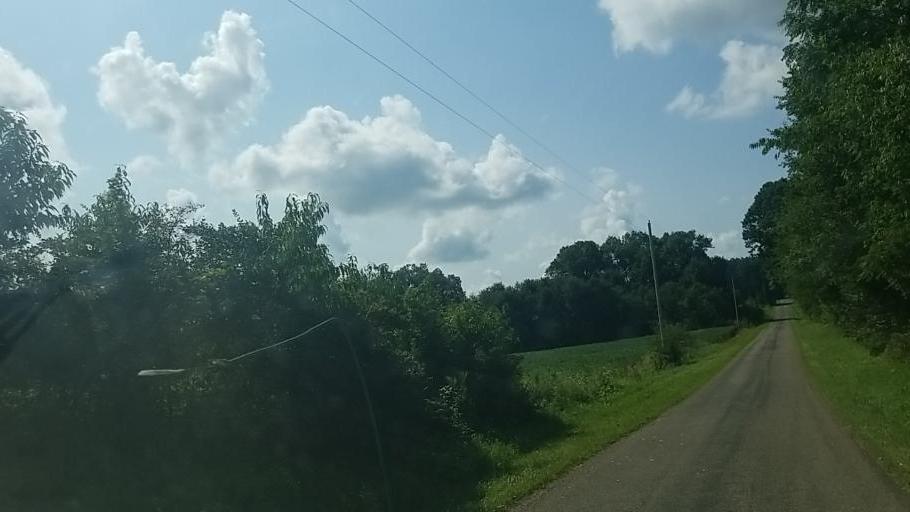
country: US
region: Ohio
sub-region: Ashland County
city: Ashland
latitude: 40.7465
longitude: -82.2979
